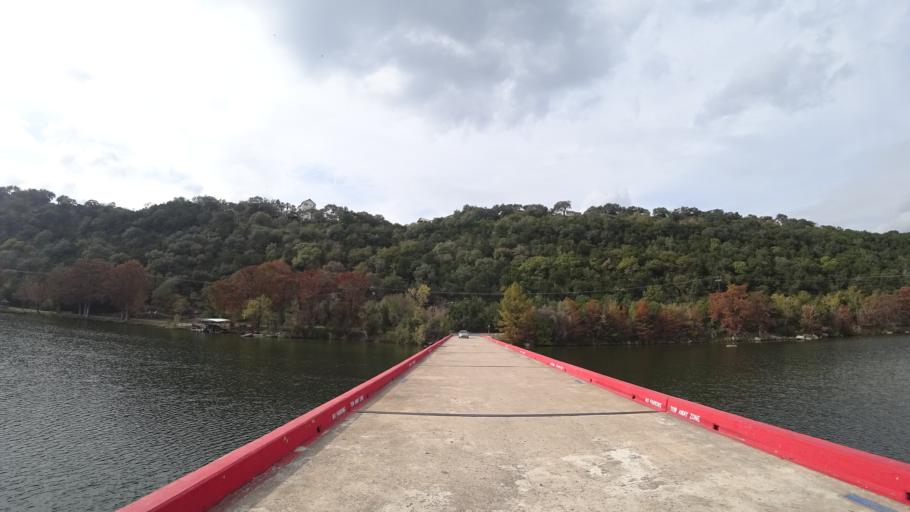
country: US
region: Texas
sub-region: Travis County
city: Hudson Bend
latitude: 30.3880
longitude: -97.9130
